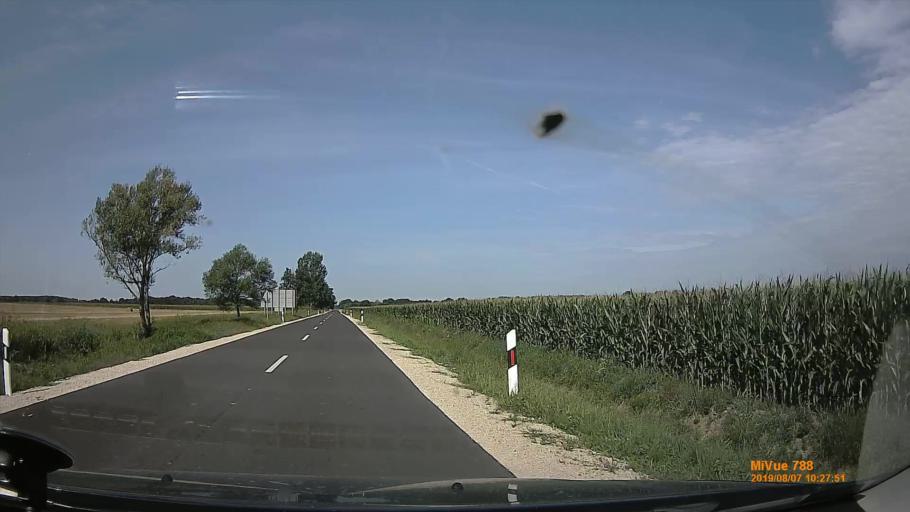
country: SI
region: Lendava-Lendva
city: Lendava
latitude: 46.6178
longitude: 16.4621
